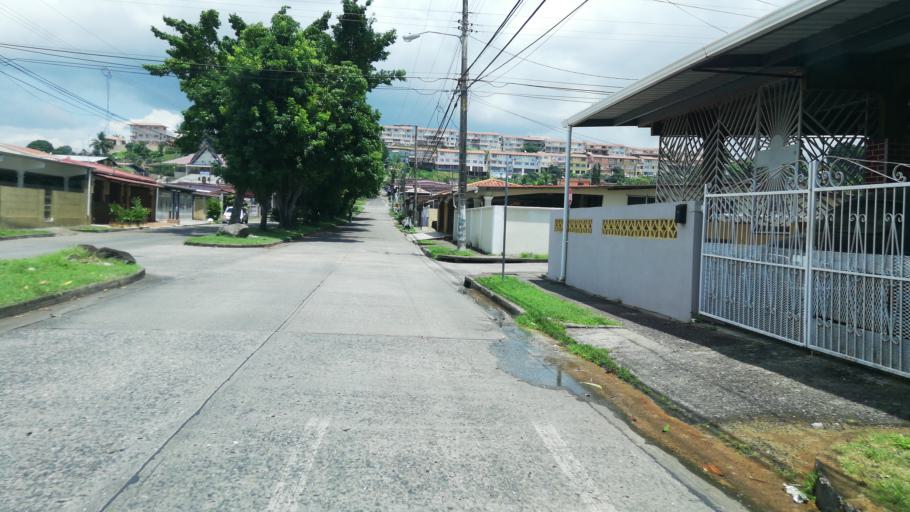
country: PA
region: Panama
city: San Miguelito
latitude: 9.0589
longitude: -79.4567
